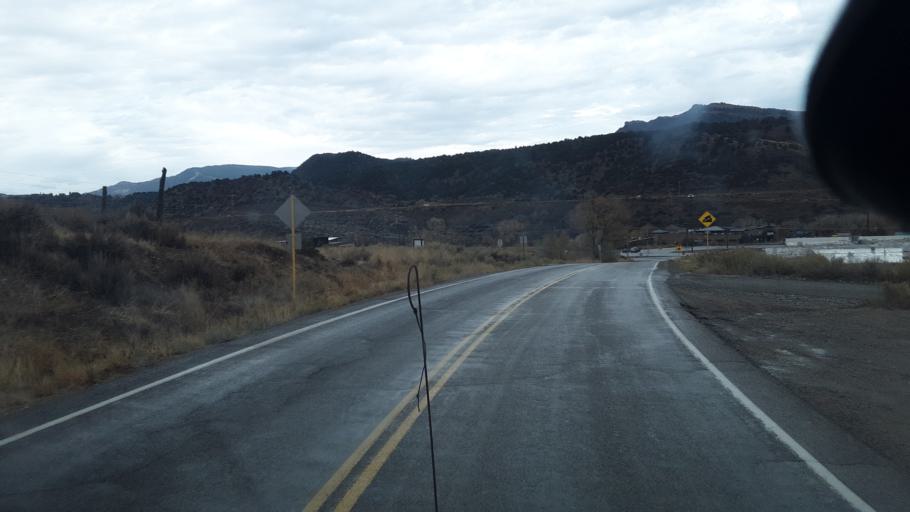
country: US
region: Colorado
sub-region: La Plata County
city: Durango
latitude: 37.2517
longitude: -107.8796
